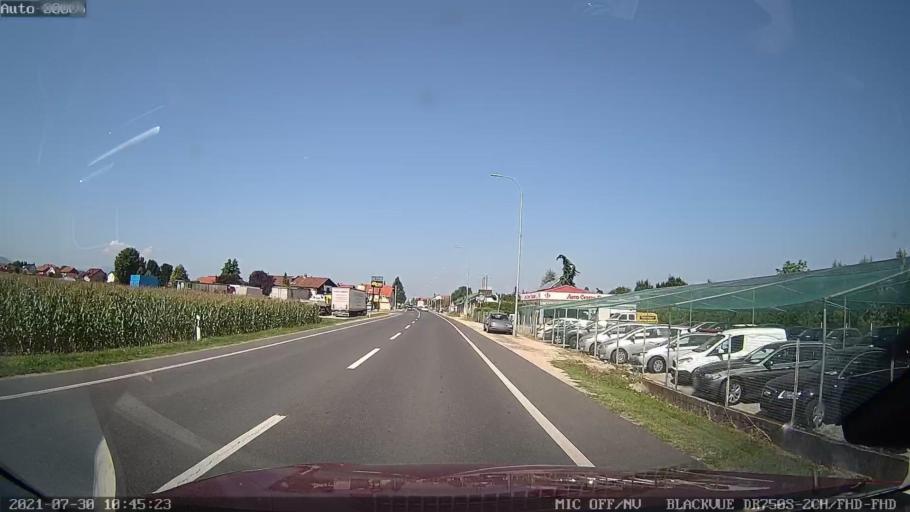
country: HR
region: Medimurska
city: Kursanec
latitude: 46.2989
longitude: 16.4058
